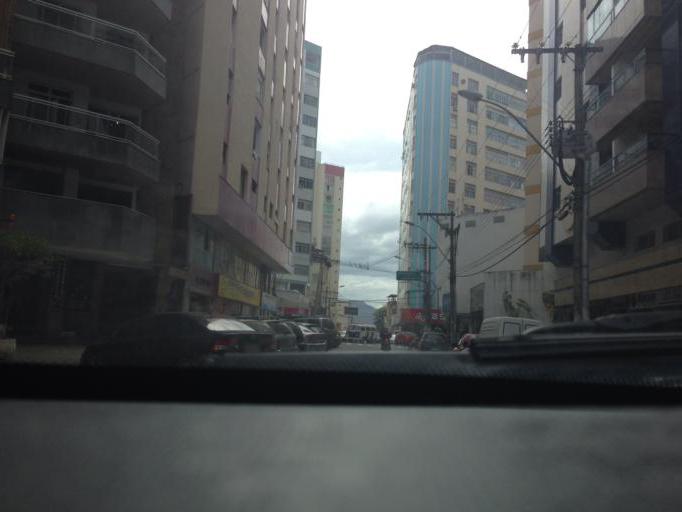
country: BR
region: Espirito Santo
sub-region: Guarapari
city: Guarapari
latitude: -20.6730
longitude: -40.4984
